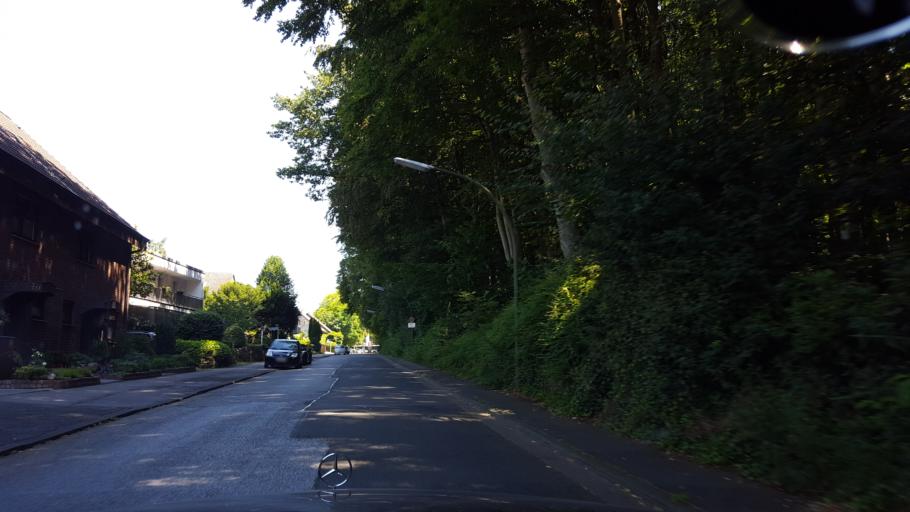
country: DE
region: North Rhine-Westphalia
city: Marl
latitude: 51.6616
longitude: 7.1332
